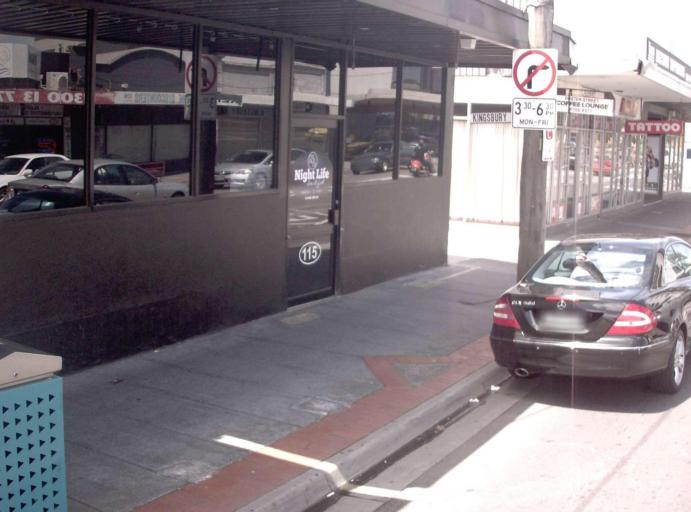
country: AU
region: Victoria
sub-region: Greater Dandenong
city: Dandenong
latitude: -37.9901
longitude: 145.2135
